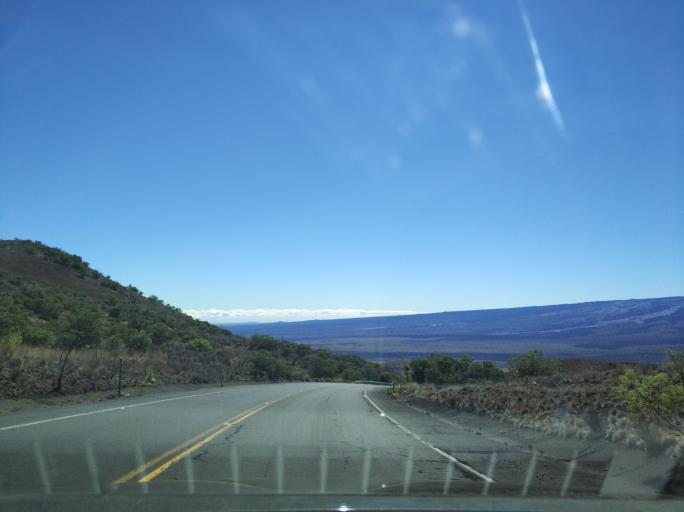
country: US
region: Hawaii
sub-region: Hawaii County
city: Honoka'a
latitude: 19.7511
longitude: -155.4552
